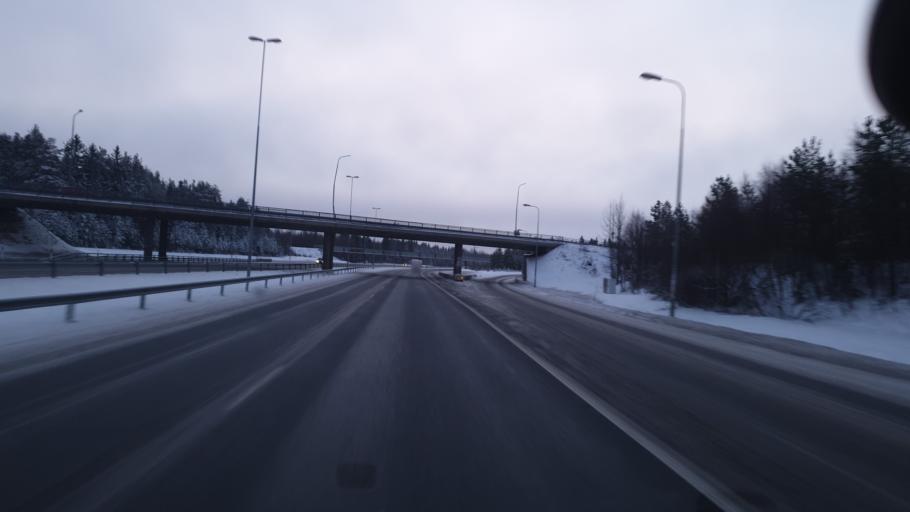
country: FI
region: Lapland
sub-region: Kemi-Tornio
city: Keminmaa
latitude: 65.7747
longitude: 24.5604
